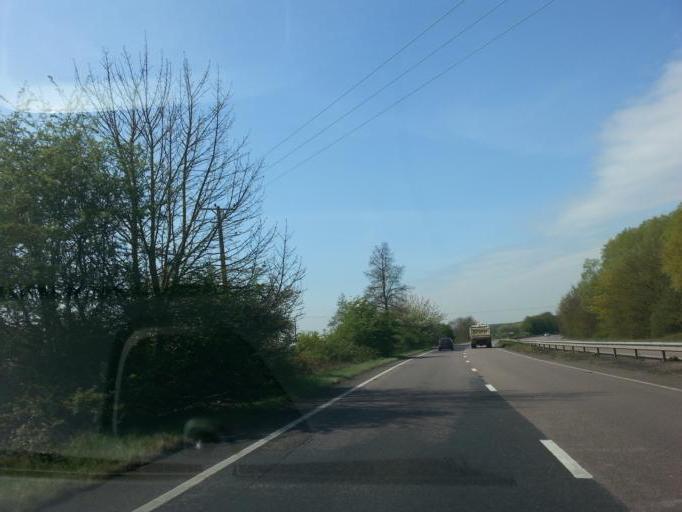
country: GB
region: England
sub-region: Suffolk
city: Wickham Market
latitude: 52.1380
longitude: 1.3665
